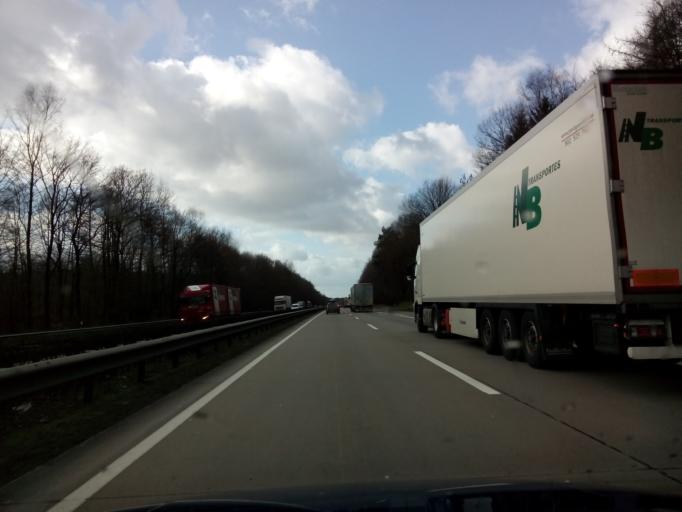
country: DE
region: Lower Saxony
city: Gross Ippener
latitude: 52.9634
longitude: 8.5922
